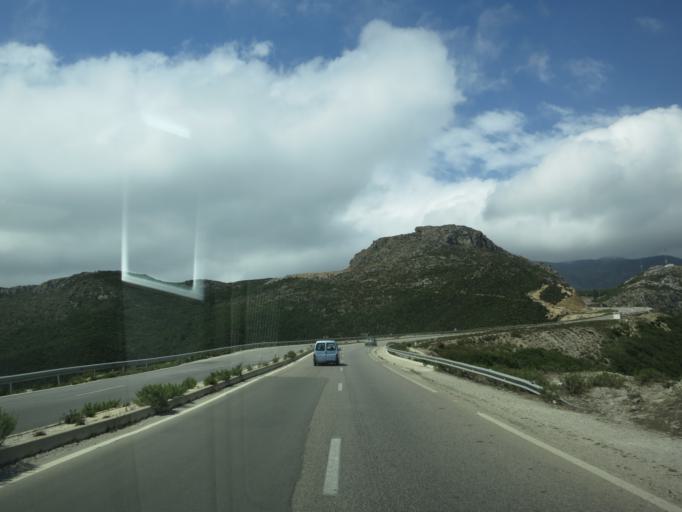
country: ES
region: Ceuta
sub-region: Ceuta
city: Ceuta
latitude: 35.8698
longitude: -5.3869
